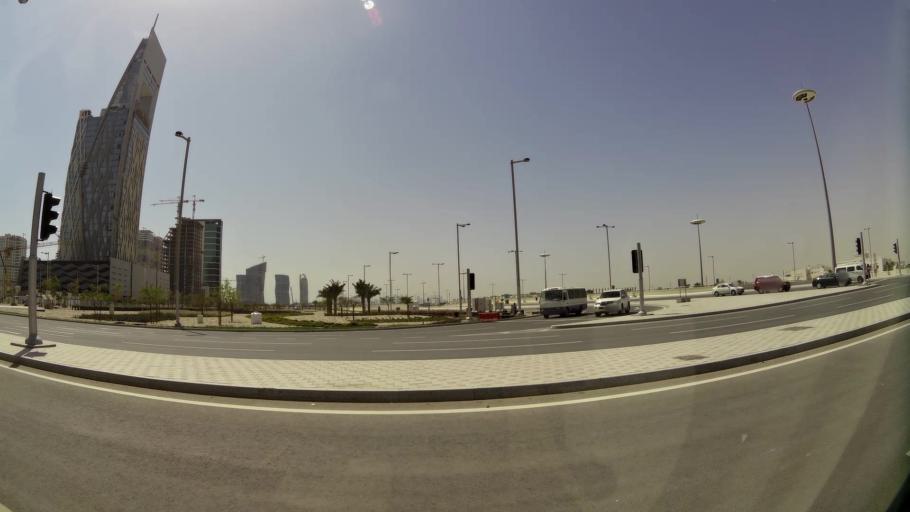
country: QA
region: Baladiyat ad Dawhah
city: Doha
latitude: 25.3936
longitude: 51.5177
